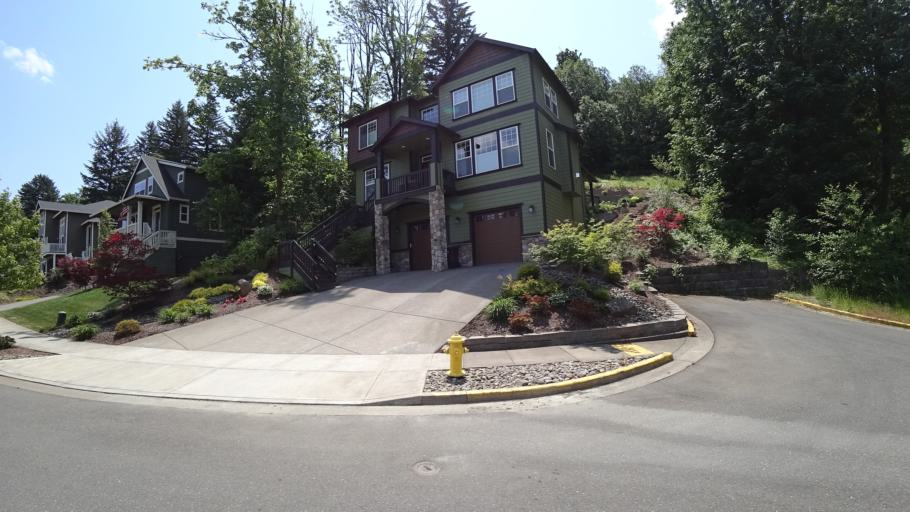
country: US
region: Oregon
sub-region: Clackamas County
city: Happy Valley
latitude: 45.4536
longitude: -122.5439
